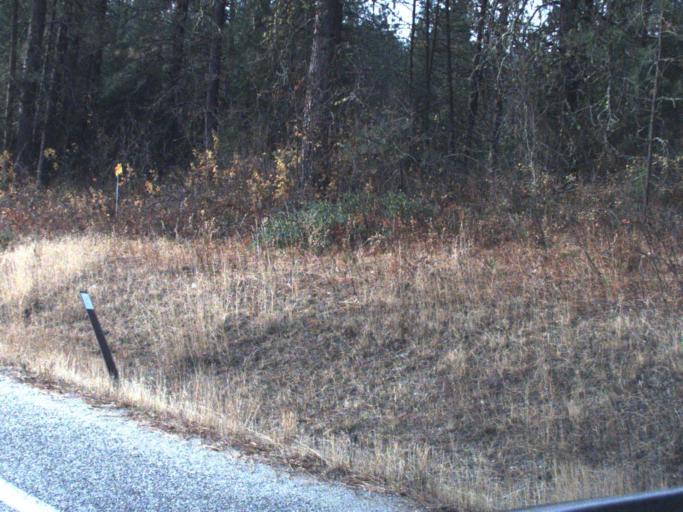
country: US
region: Washington
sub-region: Stevens County
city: Kettle Falls
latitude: 48.7722
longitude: -118.1429
